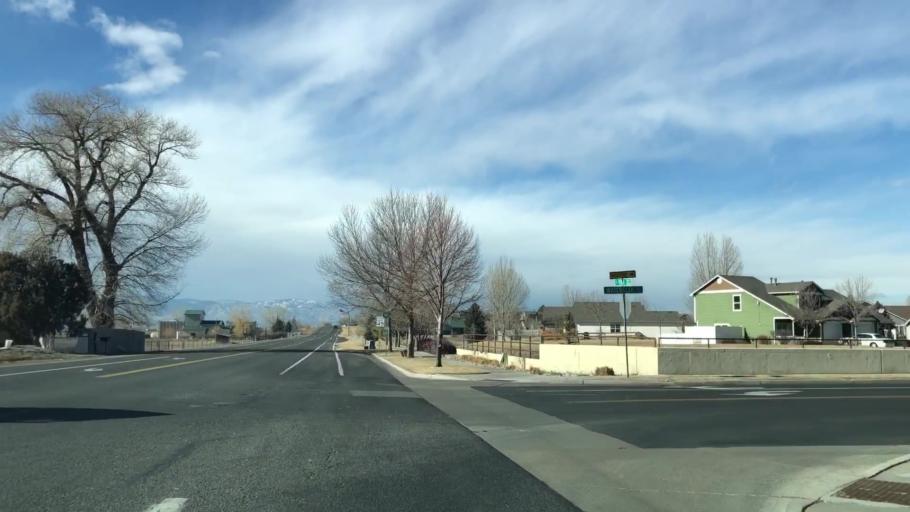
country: US
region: Colorado
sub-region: Larimer County
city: Fort Collins
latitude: 40.5958
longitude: -105.0053
